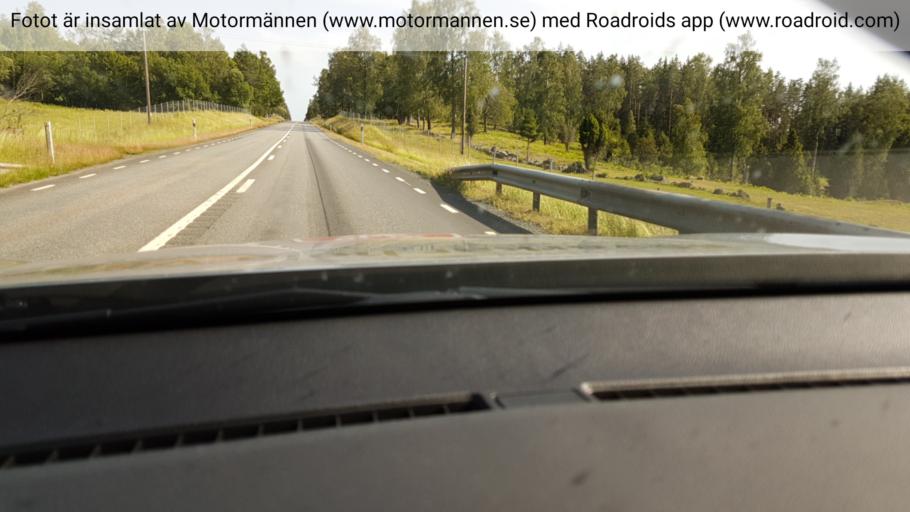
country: SE
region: Joenkoeping
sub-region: Eksjo Kommun
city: Eksjoe
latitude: 57.7240
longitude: 14.9372
